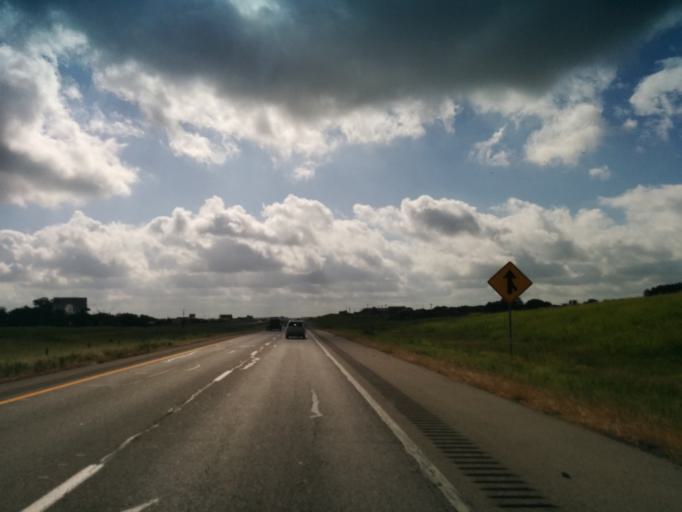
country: US
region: Texas
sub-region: Caldwell County
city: Luling
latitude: 29.6510
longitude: -97.6600
